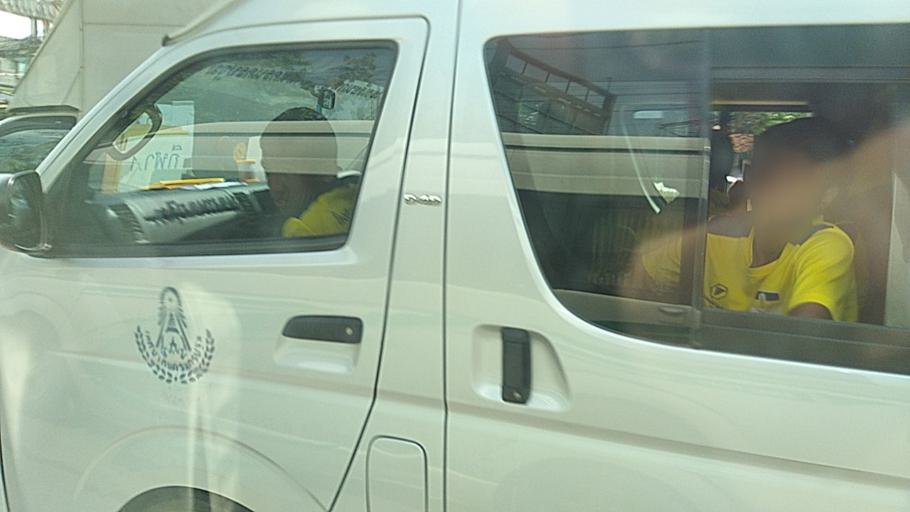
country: TH
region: Bangkok
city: Lak Si
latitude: 13.8987
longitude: 100.5446
